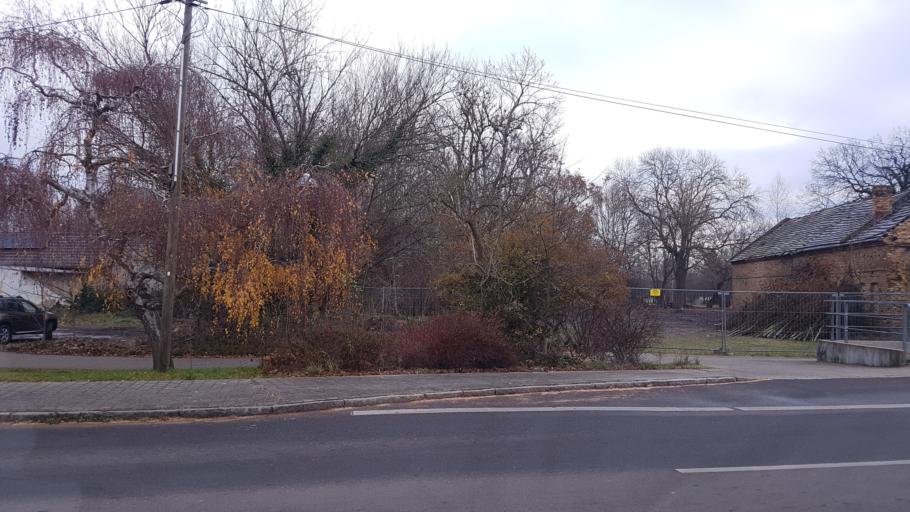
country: DE
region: Brandenburg
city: Schipkau
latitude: 51.5423
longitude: 13.8948
